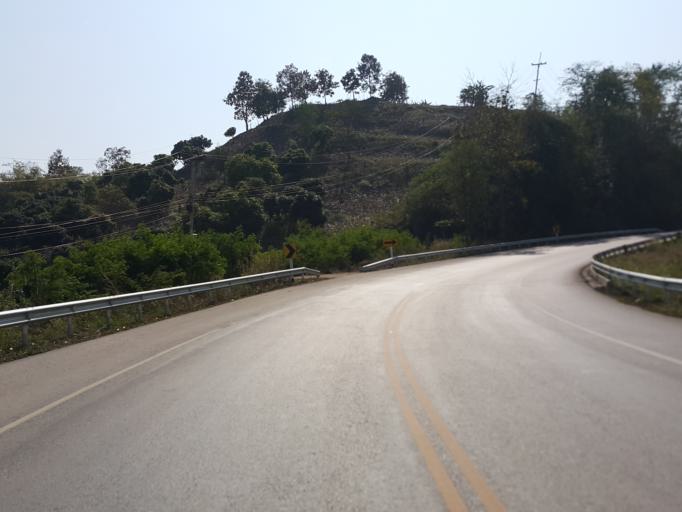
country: TH
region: Lampang
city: Mueang Pan
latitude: 18.8939
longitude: 99.6061
